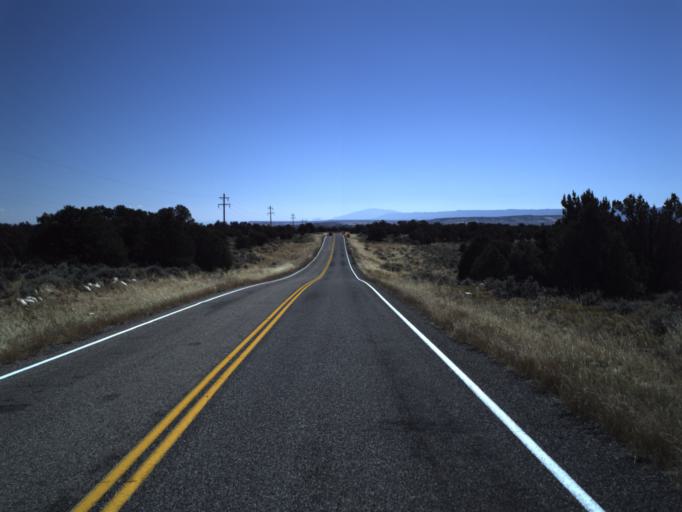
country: US
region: Utah
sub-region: Wayne County
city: Loa
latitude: 37.8547
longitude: -111.4329
